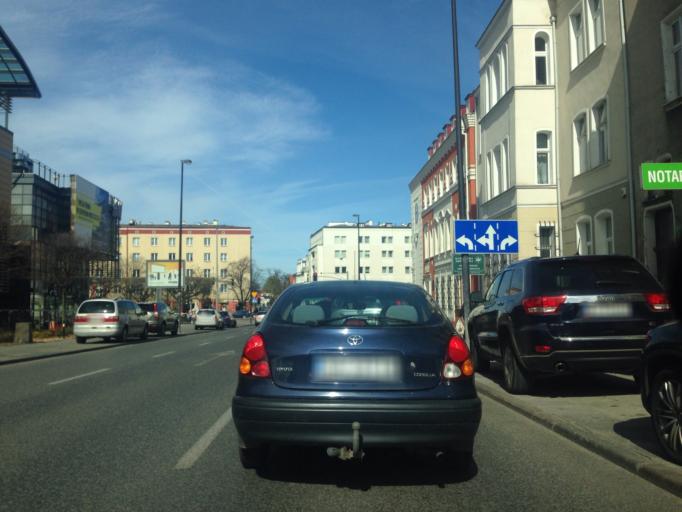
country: PL
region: Pomeranian Voivodeship
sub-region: Gdansk
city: Gdansk
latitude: 54.3768
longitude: 18.6079
